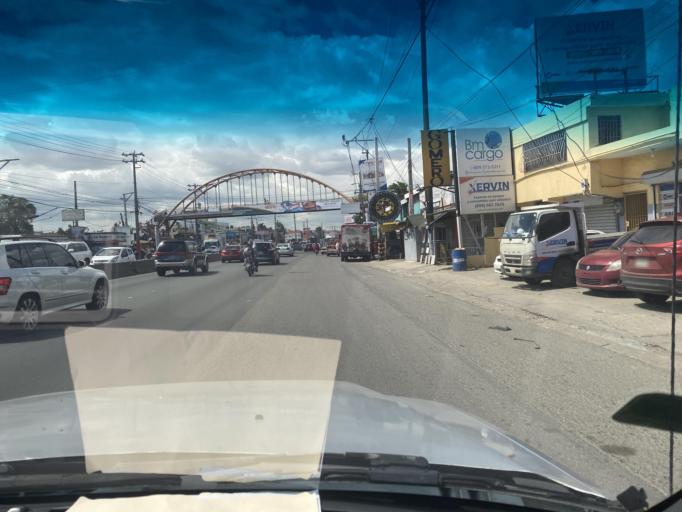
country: DO
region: Santo Domingo
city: Santo Domingo Oeste
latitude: 18.5104
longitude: -70.0077
